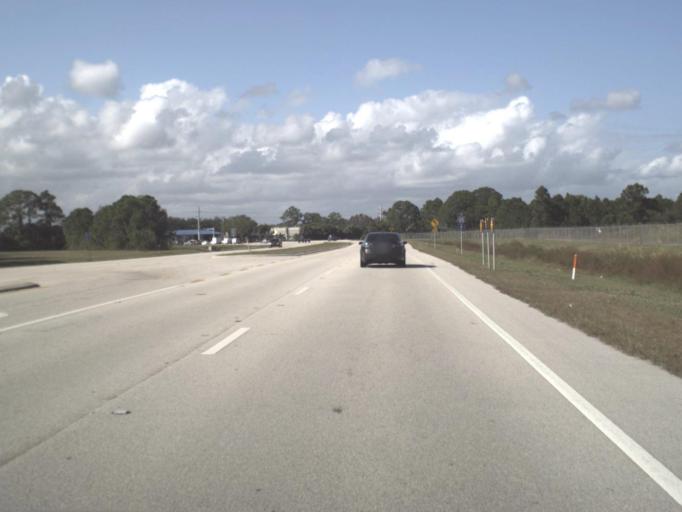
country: US
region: Florida
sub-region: Brevard County
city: June Park
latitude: 28.0987
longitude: -80.6685
